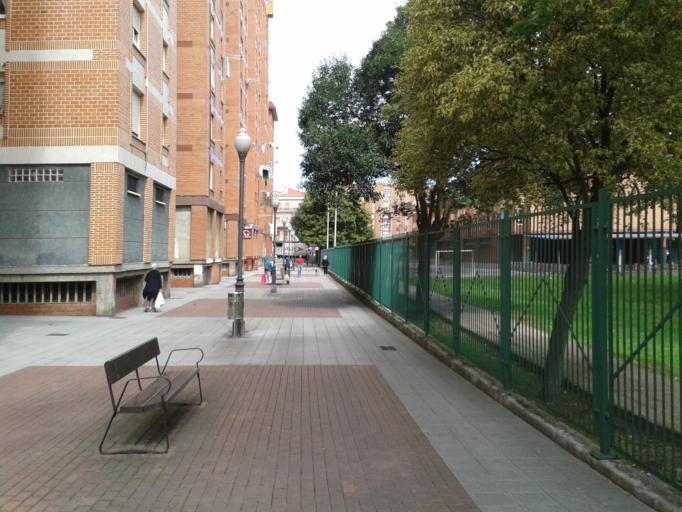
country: ES
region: Asturias
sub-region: Province of Asturias
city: Natahoyo
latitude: 43.5378
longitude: -5.6845
